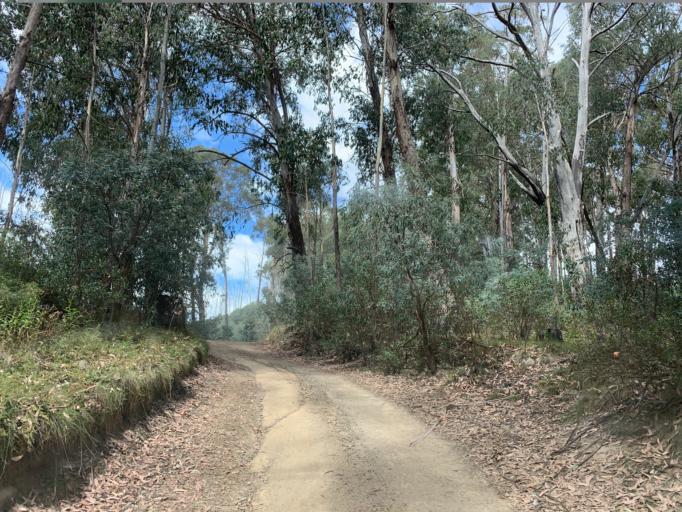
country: AU
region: Victoria
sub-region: Mansfield
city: Mansfield
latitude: -37.0982
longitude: 146.5436
